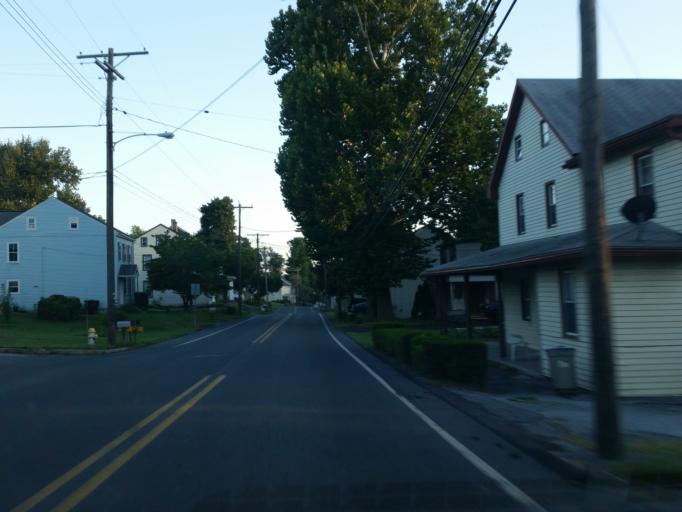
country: US
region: Pennsylvania
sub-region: Lebanon County
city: Sand Hill
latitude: 40.3606
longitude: -76.4324
